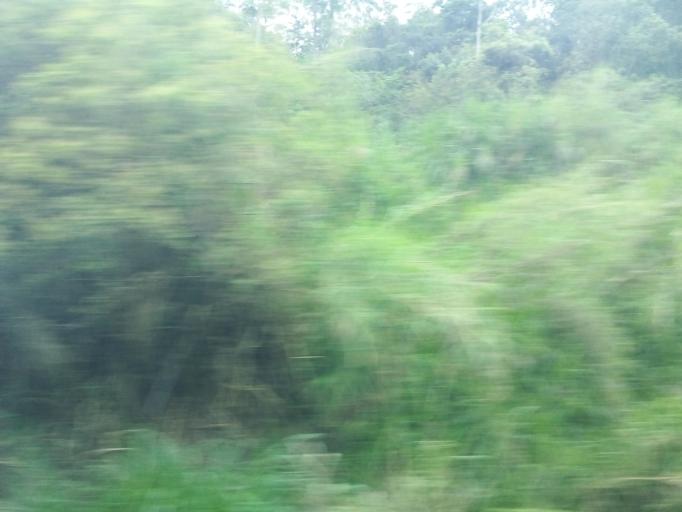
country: BR
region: Minas Gerais
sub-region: Rio Piracicaba
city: Rio Piracicaba
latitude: -19.8899
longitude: -43.1379
